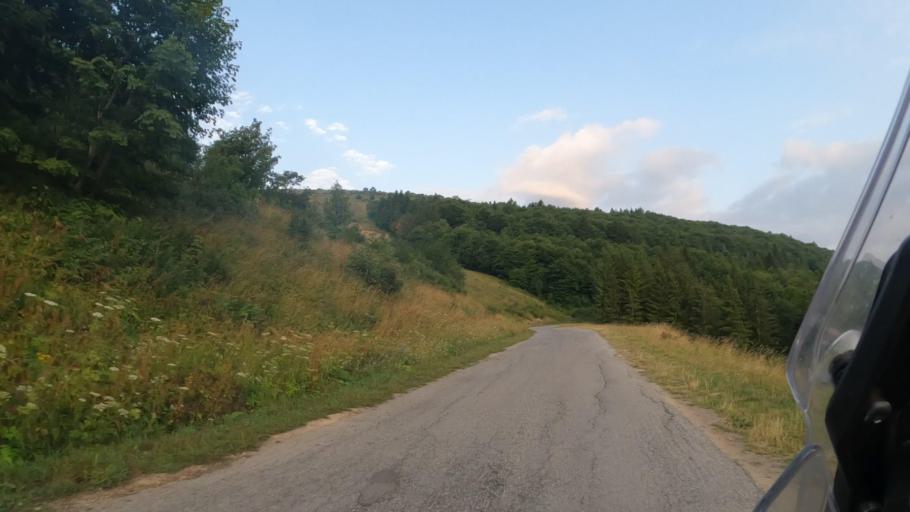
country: IT
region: Piedmont
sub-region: Provincia di Cuneo
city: Limone Piemonte
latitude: 44.1609
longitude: 7.5694
